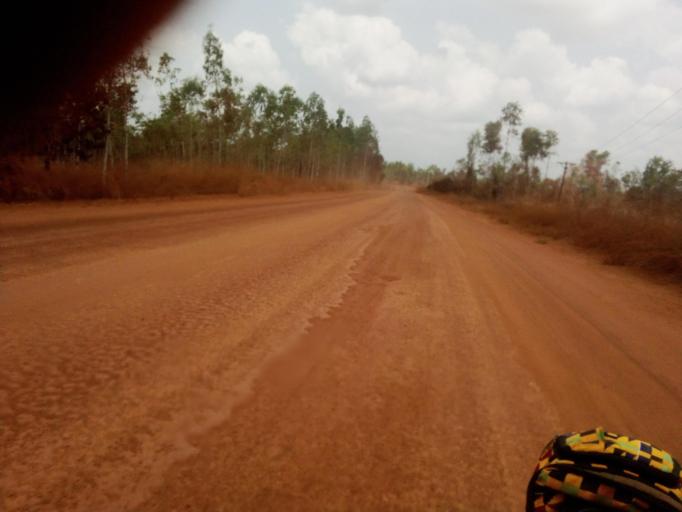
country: SL
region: Southern Province
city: Mogbwemo
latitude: 7.7548
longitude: -12.2938
